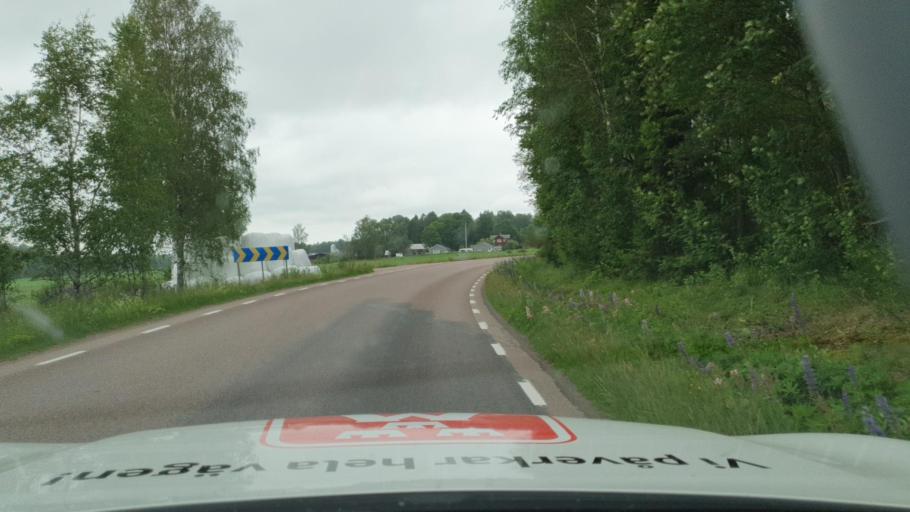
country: SE
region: Vaermland
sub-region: Kristinehamns Kommun
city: Kristinehamn
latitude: 59.4806
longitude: 13.9370
